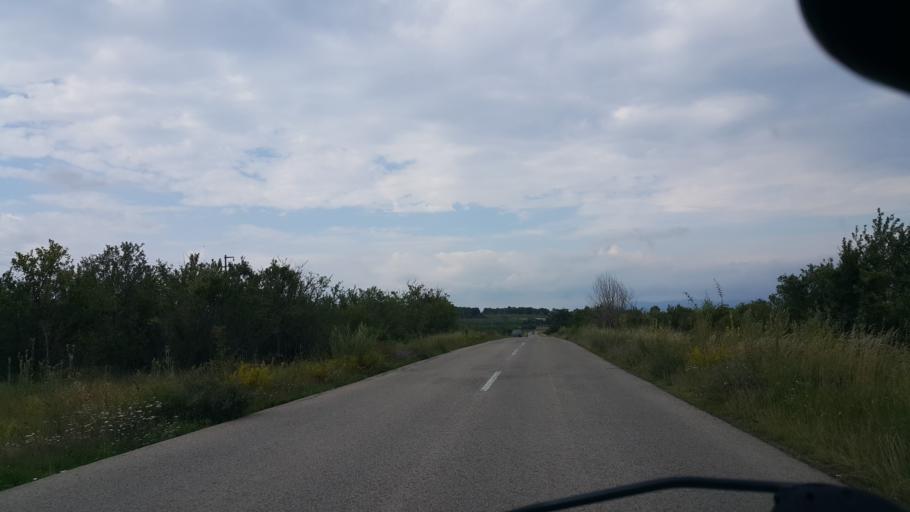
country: RS
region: Central Serbia
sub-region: Toplicki Okrug
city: Blace
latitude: 43.2443
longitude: 21.2579
